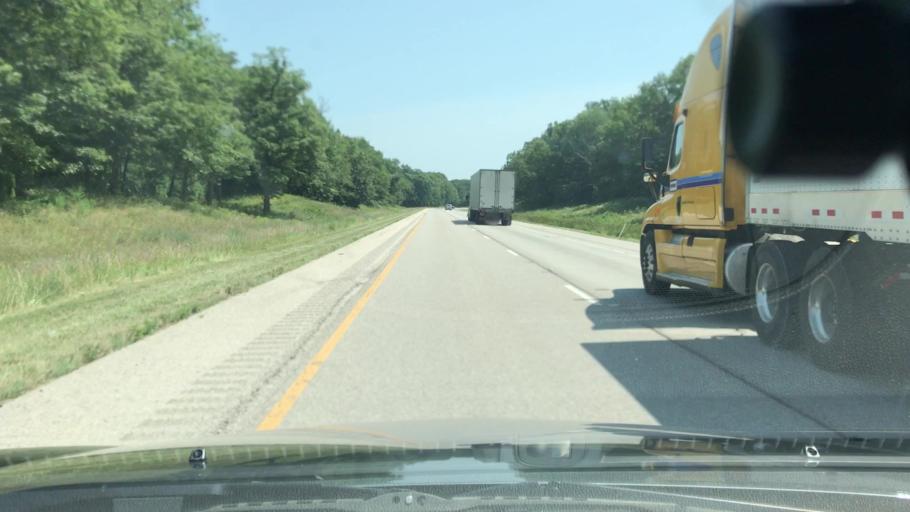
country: US
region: Illinois
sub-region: Washington County
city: Nashville
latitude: 38.3903
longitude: -89.3234
